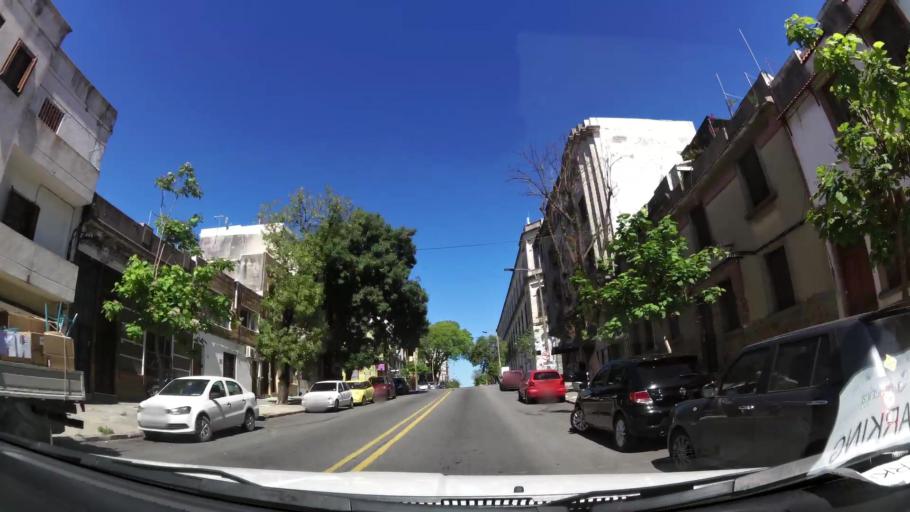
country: UY
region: Montevideo
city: Montevideo
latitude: -34.9122
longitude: -56.1776
